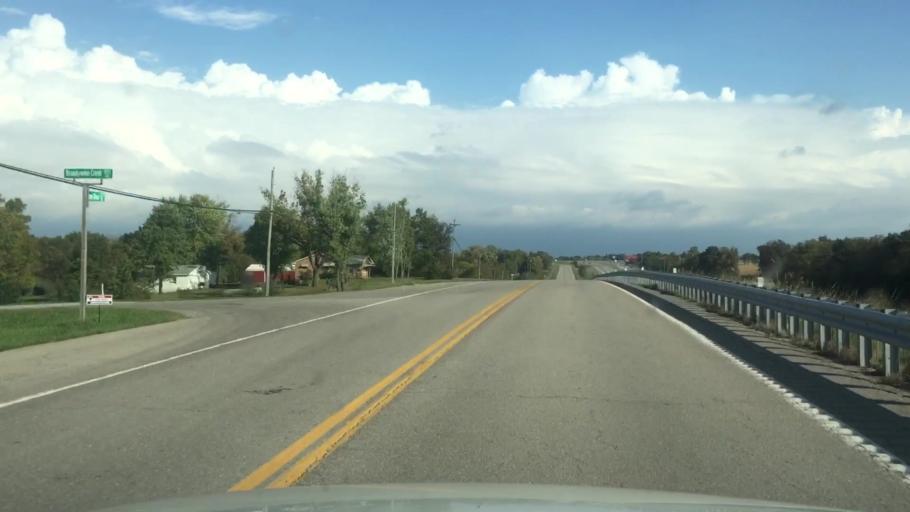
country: US
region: Missouri
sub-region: Boone County
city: Ashland
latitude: 38.8498
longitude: -92.2500
